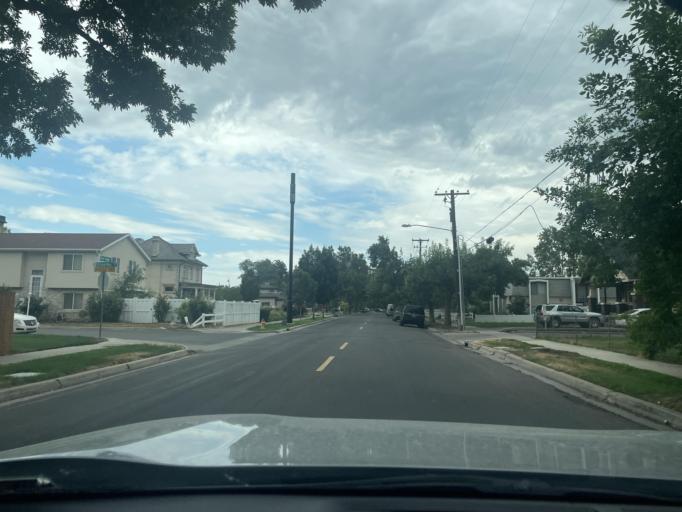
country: US
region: Utah
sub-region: Salt Lake County
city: South Salt Lake
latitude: 40.7302
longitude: -111.8940
